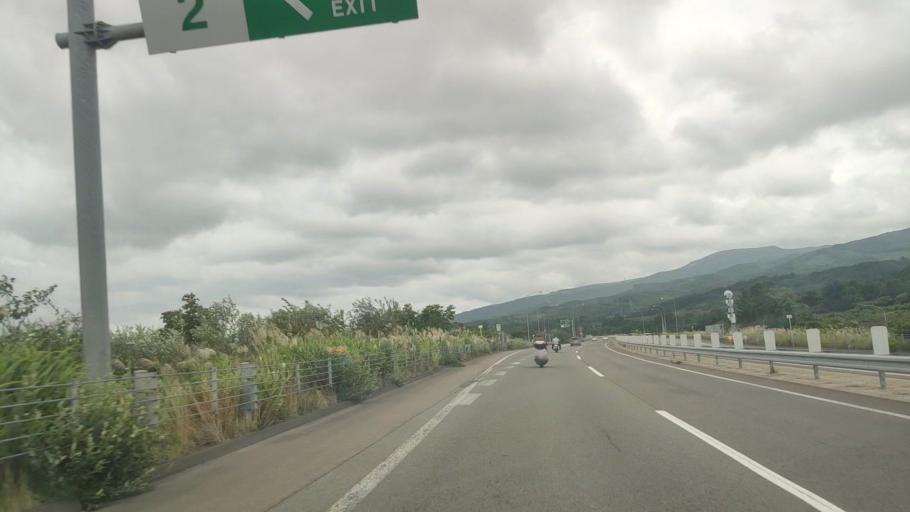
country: JP
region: Hokkaido
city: Nanae
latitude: 41.8645
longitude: 140.7307
